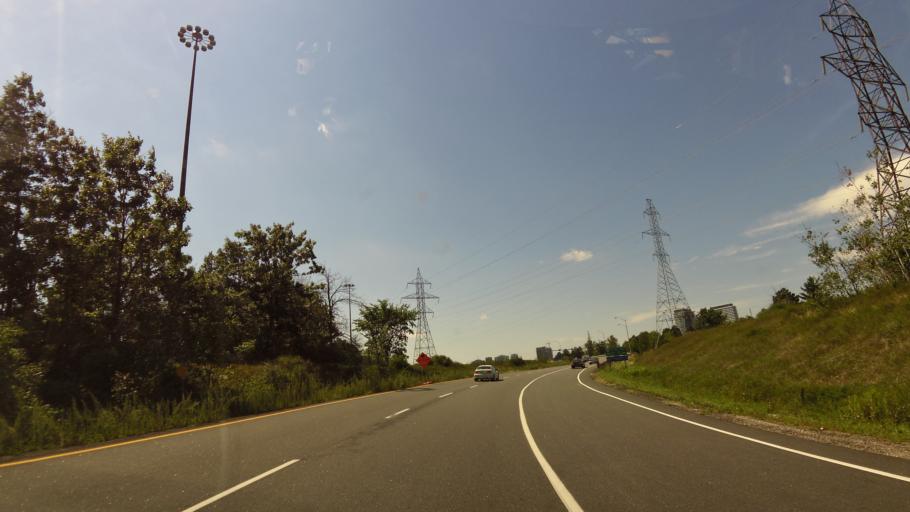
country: CA
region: Ontario
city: Mississauga
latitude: 43.5559
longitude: -79.6947
